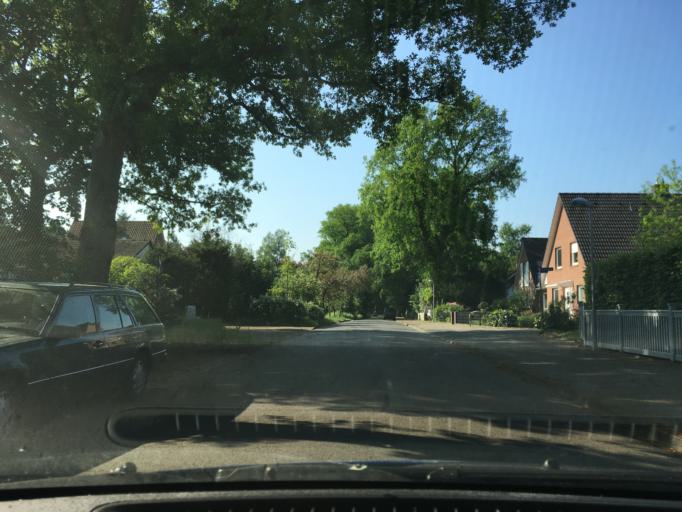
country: DE
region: Lower Saxony
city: Lueneburg
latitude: 53.2305
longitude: 10.4218
